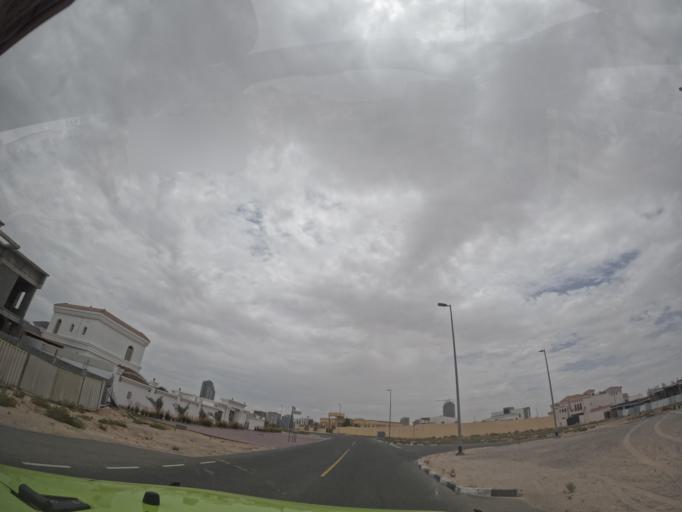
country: AE
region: Dubai
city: Dubai
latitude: 25.1265
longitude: 55.3648
